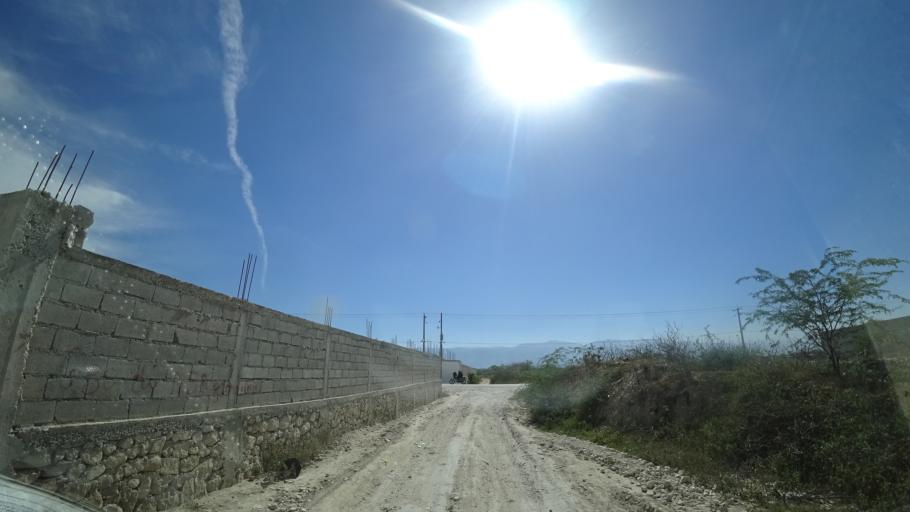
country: HT
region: Ouest
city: Croix des Bouquets
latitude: 18.6490
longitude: -72.2495
